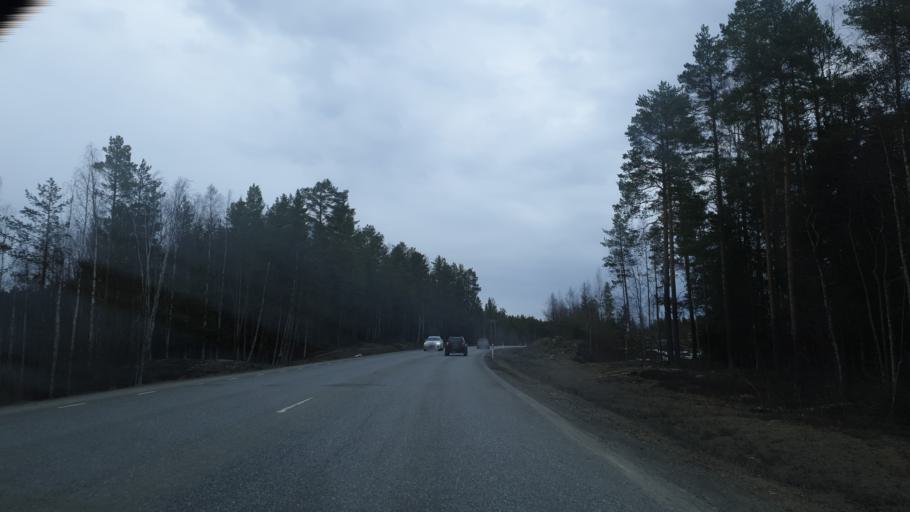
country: SE
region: Vaesterbotten
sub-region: Skelleftea Kommun
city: Viken
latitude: 64.7054
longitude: 20.9420
